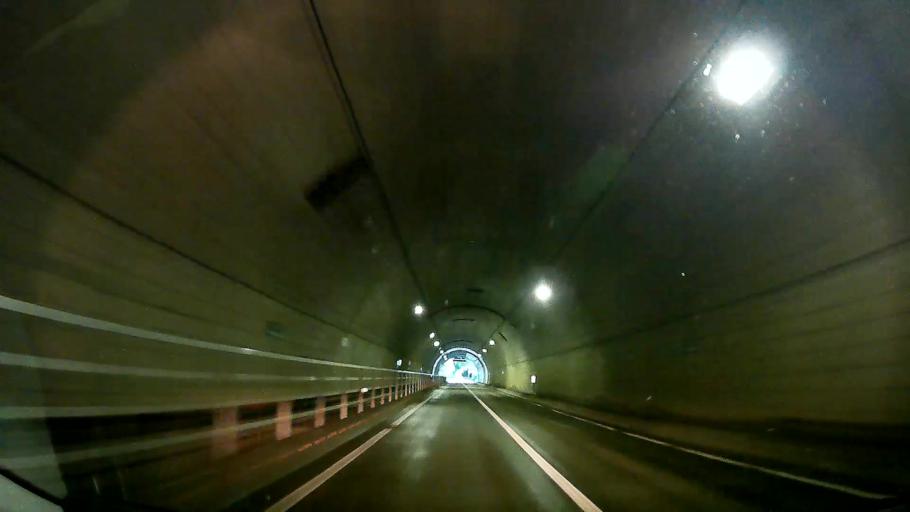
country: JP
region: Hokkaido
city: Sapporo
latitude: 42.9823
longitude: 141.1506
